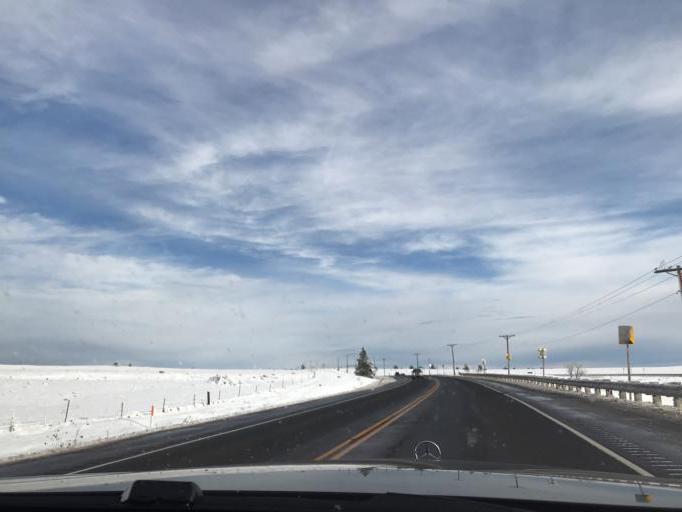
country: US
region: Colorado
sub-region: Boulder County
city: Superior
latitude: 39.9250
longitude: -105.2345
